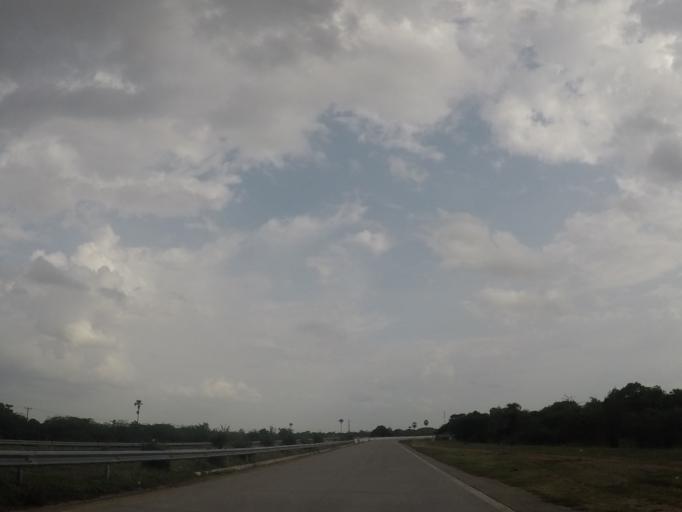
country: MM
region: Mandalay
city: Meiktila
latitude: 20.7915
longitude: 95.7703
